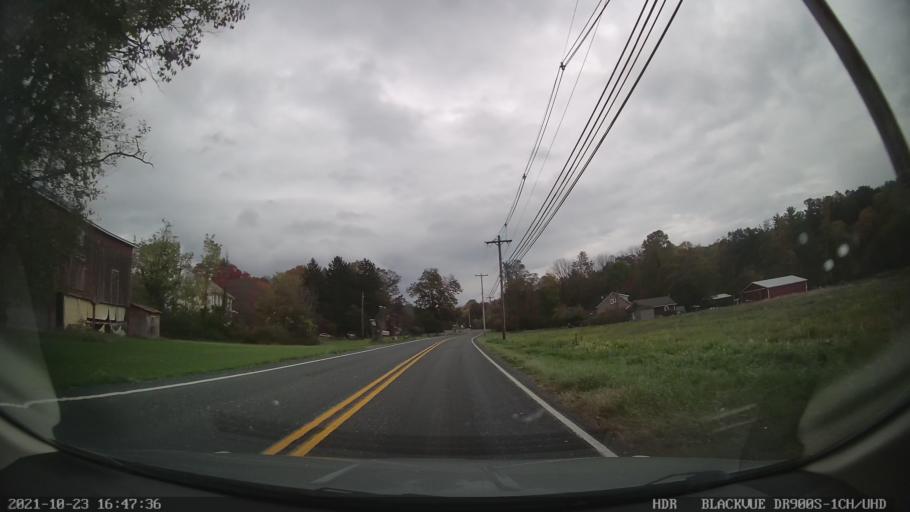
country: US
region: Pennsylvania
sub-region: Berks County
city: Red Lion
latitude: 40.4900
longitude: -75.6356
